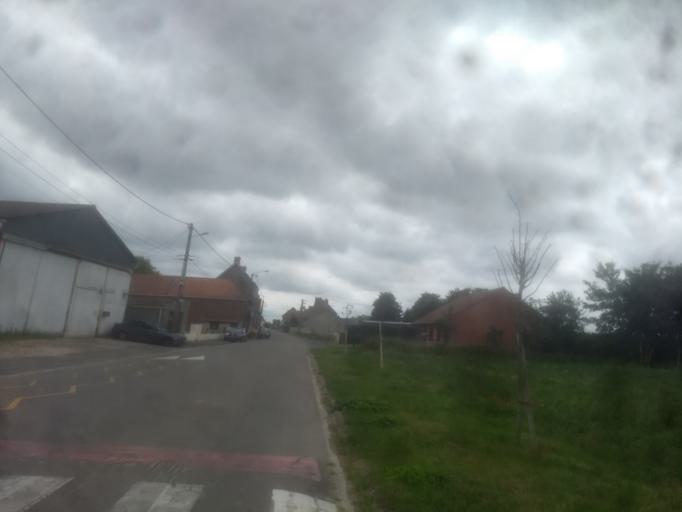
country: FR
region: Nord-Pas-de-Calais
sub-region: Departement du Pas-de-Calais
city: Thelus
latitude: 50.3290
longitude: 2.7912
